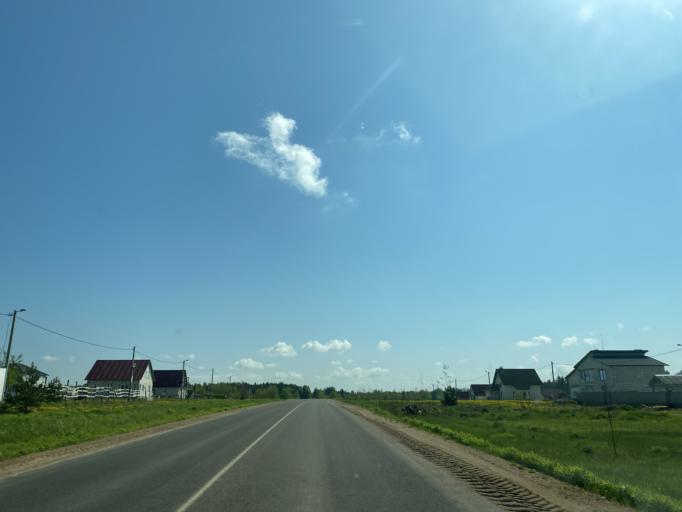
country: BY
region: Minsk
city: Horad Barysaw
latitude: 54.1791
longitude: 28.5622
